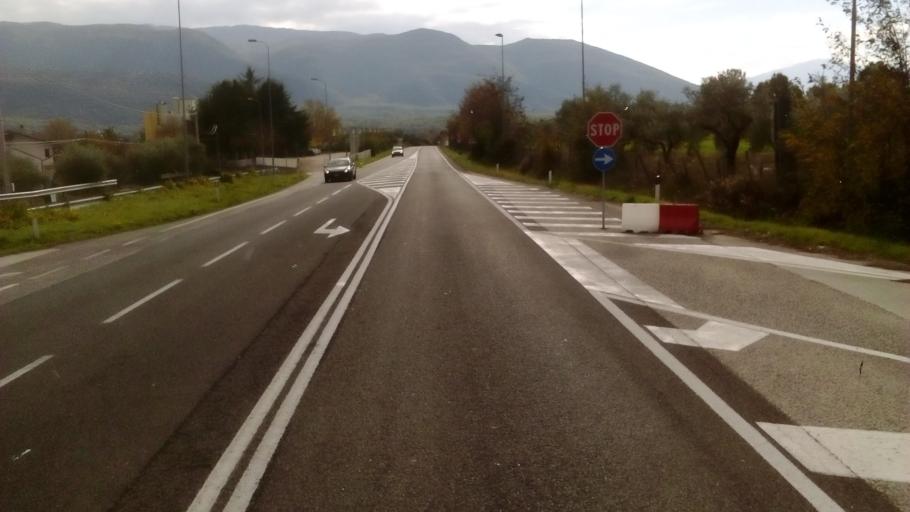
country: IT
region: Molise
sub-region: Provincia di Isernia
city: Macchia d'Isernia
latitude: 41.5404
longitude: 14.1579
